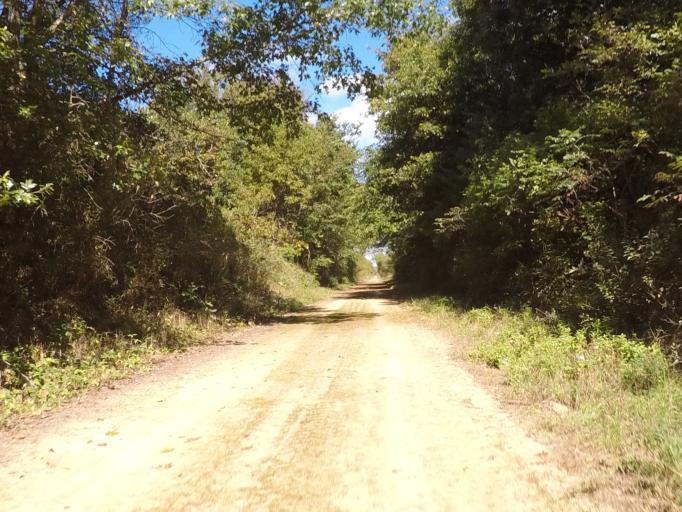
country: US
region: Wisconsin
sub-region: Richland County
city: Richland Center
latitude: 43.2283
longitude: -90.2985
